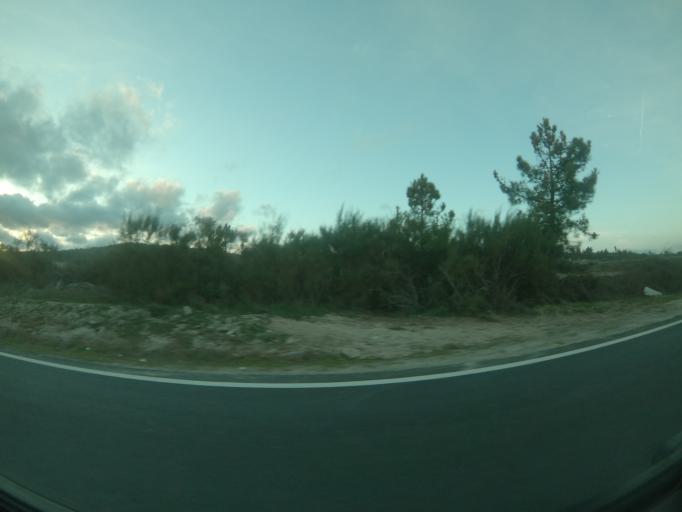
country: PT
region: Braganca
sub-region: Carrazeda de Ansiaes
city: Carrazeda de Anciaes
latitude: 41.2509
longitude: -7.2868
